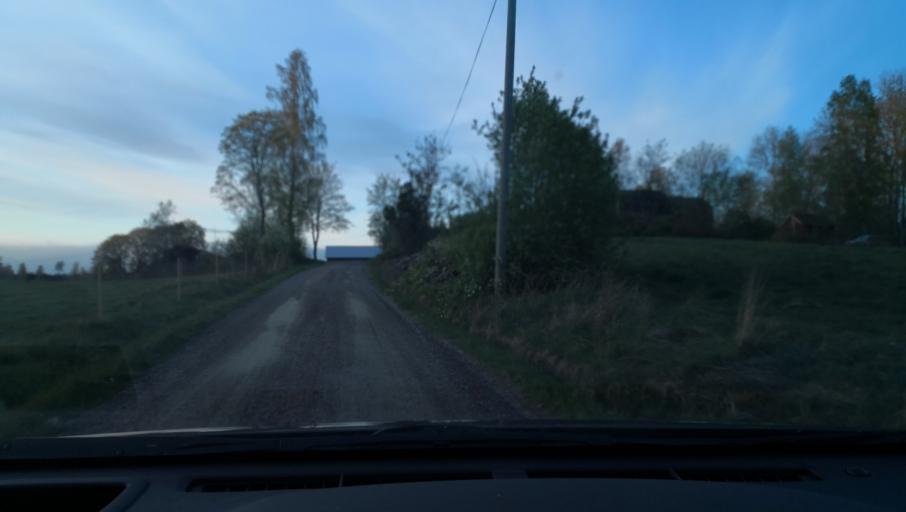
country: SE
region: OErebro
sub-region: Askersunds Kommun
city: Asbro
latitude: 58.9789
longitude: 14.9492
